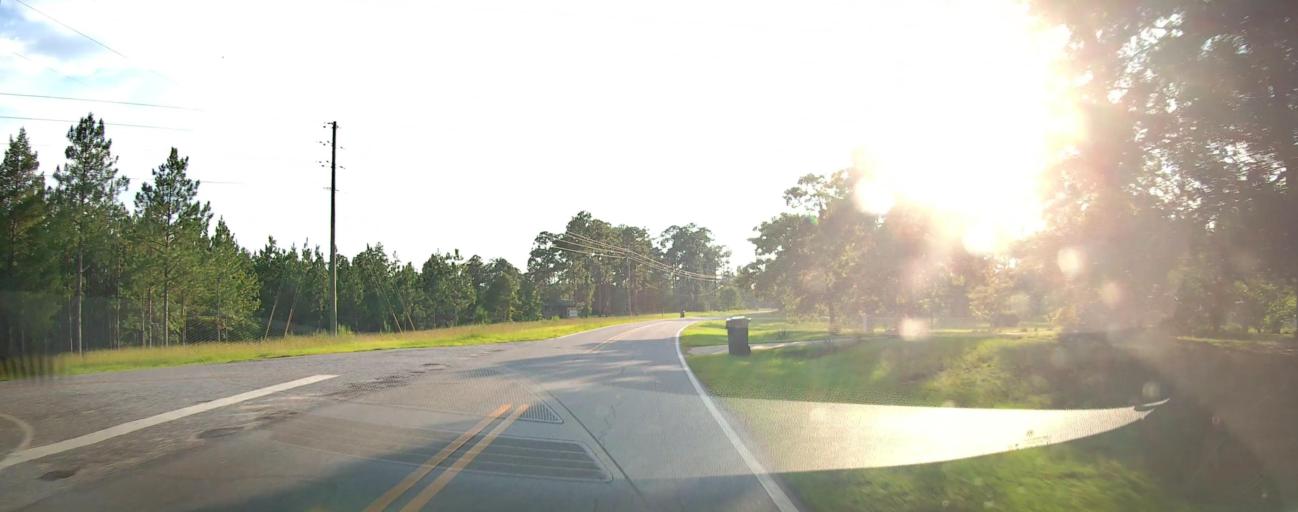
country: US
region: Georgia
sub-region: Peach County
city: Byron
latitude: 32.7042
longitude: -83.8182
